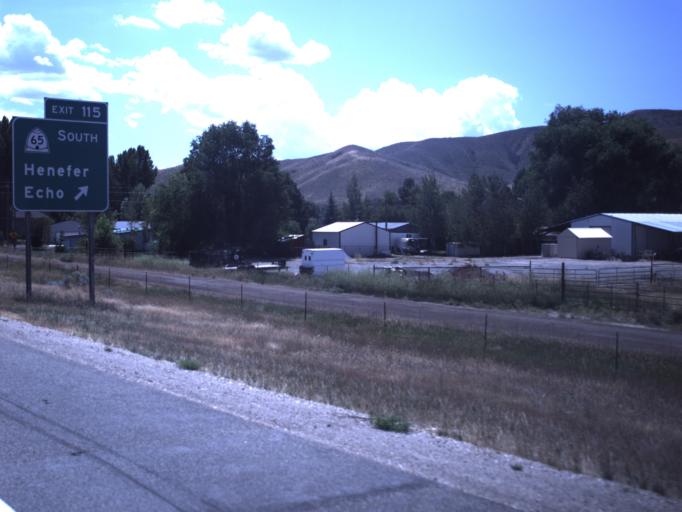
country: US
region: Utah
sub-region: Summit County
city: Coalville
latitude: 41.0201
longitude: -111.4931
